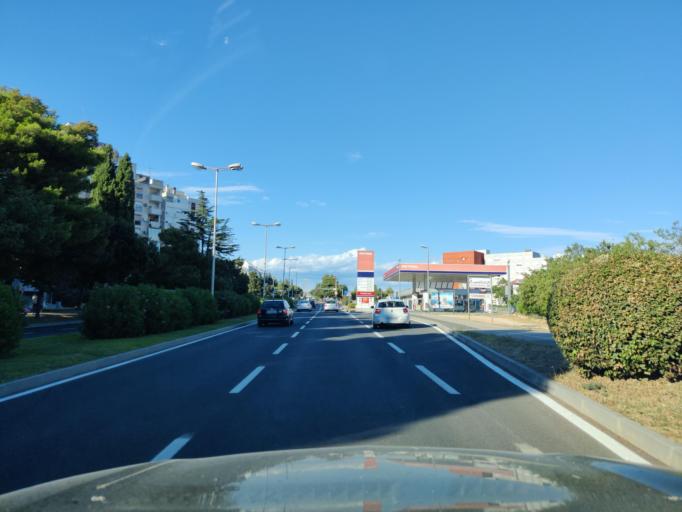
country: HR
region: Zadarska
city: Zadar
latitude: 44.1100
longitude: 15.2474
